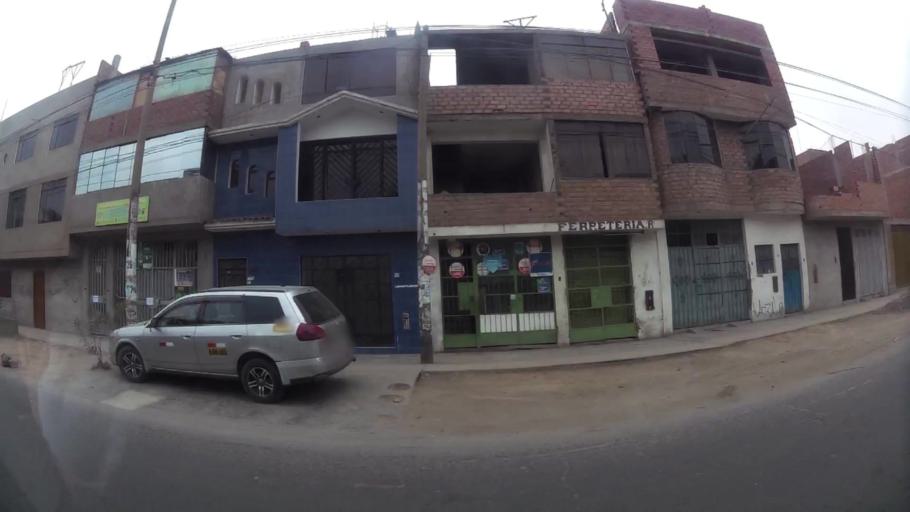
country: PE
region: Lima
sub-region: Lima
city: Independencia
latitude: -11.9555
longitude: -77.0759
